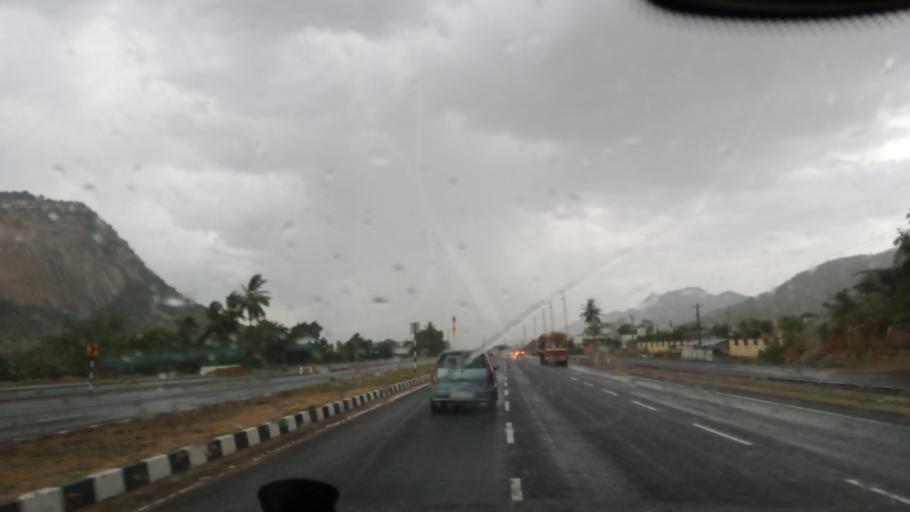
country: IN
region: Andhra Pradesh
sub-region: Chittoor
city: Narasingapuram
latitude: 13.5801
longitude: 79.2856
